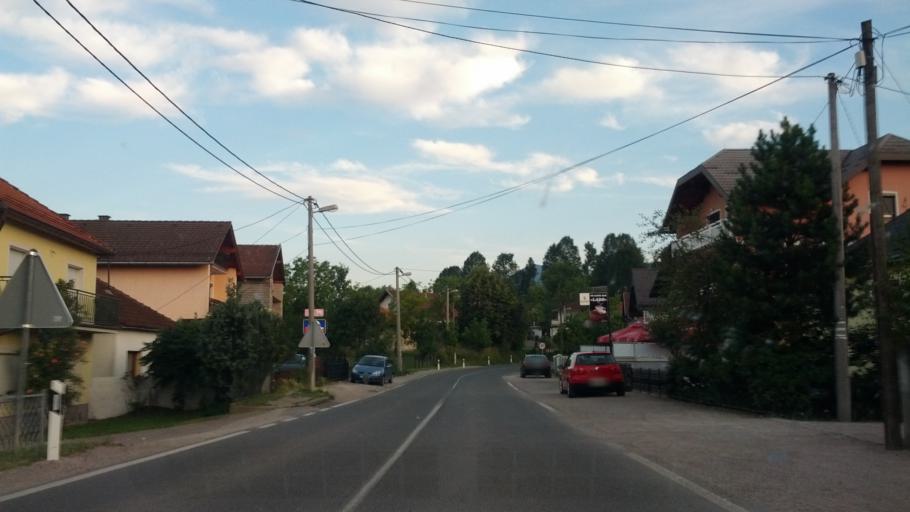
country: BA
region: Federation of Bosnia and Herzegovina
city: Izacic
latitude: 44.8747
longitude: 15.7825
